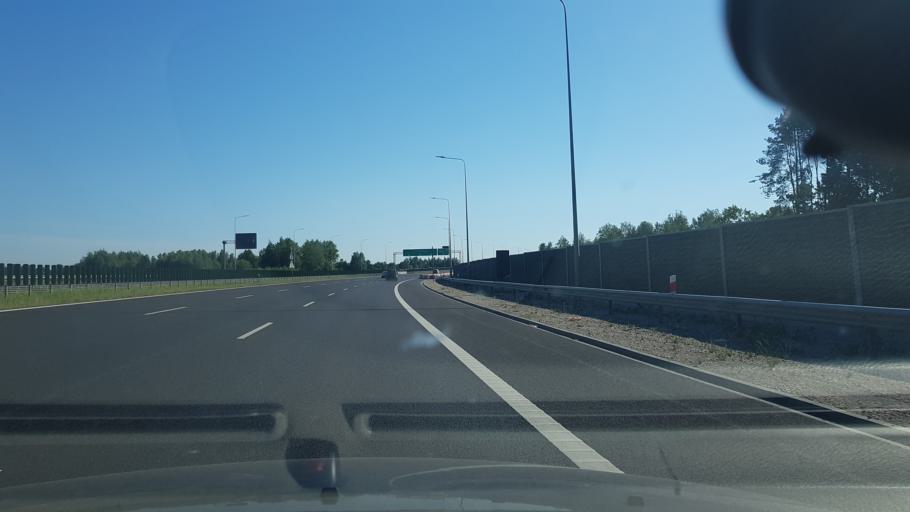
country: PL
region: Masovian Voivodeship
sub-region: Powiat wolominski
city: Slupno
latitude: 52.3486
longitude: 21.1586
